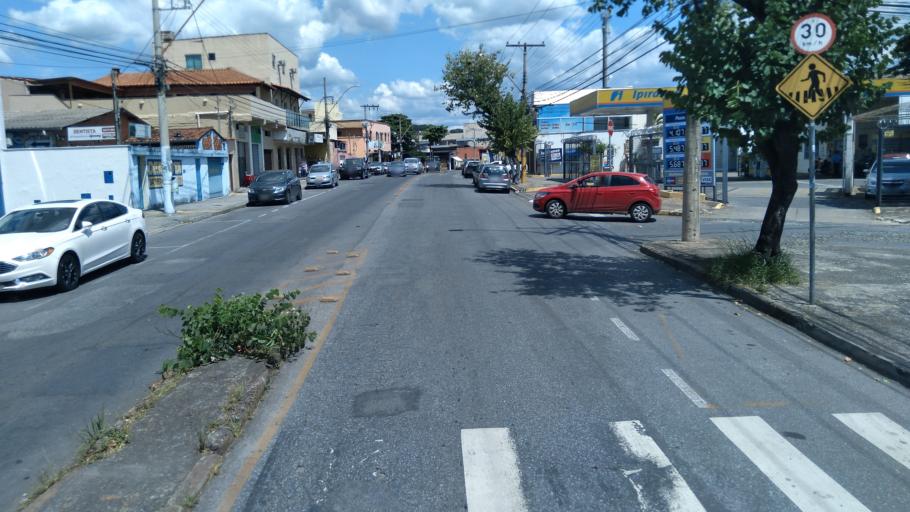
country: BR
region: Minas Gerais
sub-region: Contagem
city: Contagem
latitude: -19.9080
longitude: -43.9988
